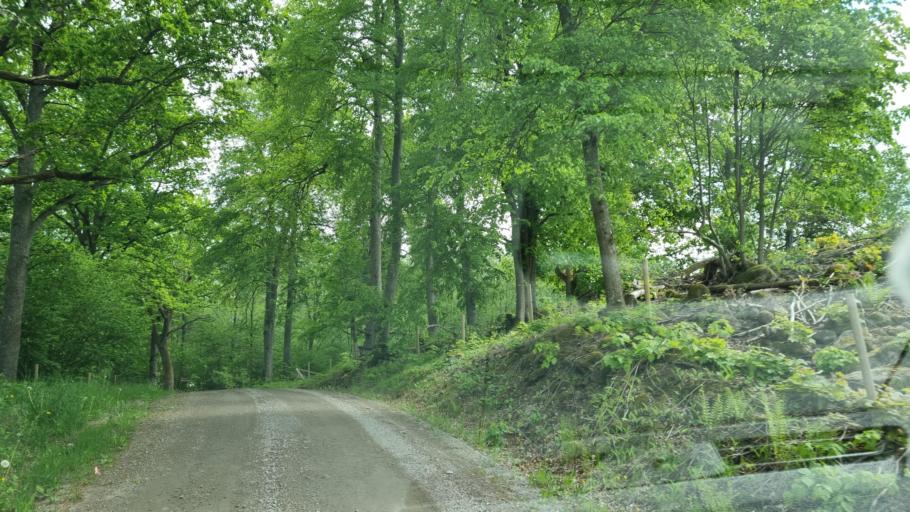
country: SE
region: OEstergoetland
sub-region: Atvidabergs Kommun
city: Atvidaberg
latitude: 58.1904
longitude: 16.0389
